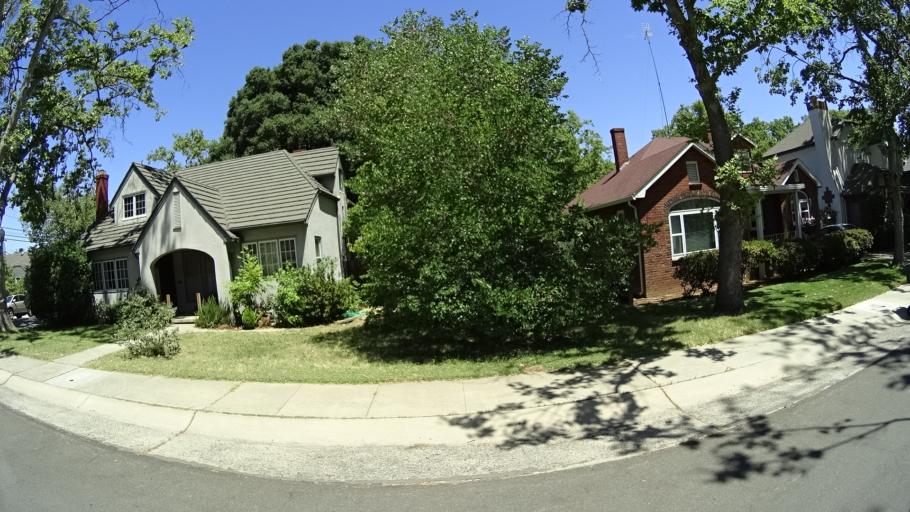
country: US
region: California
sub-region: Sacramento County
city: Sacramento
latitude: 38.5445
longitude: -121.4819
